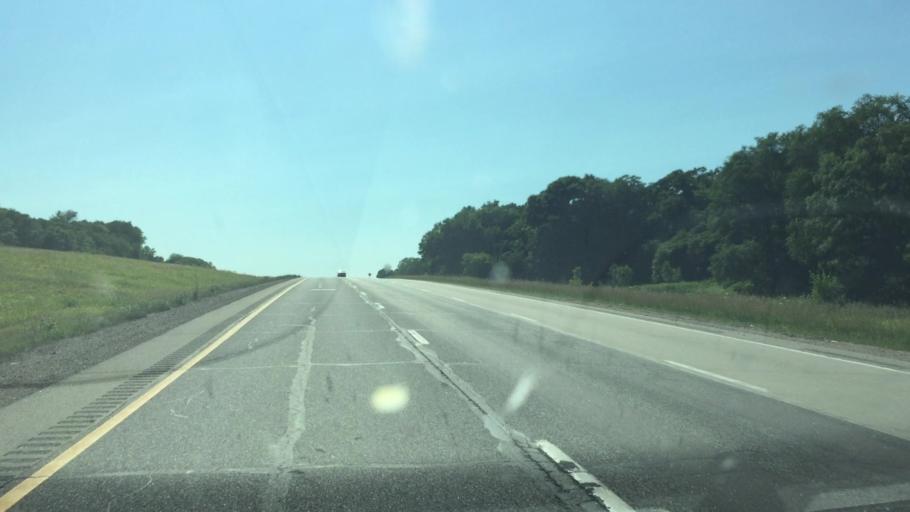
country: US
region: Iowa
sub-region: Linn County
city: Ely
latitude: 41.9259
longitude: -91.5605
